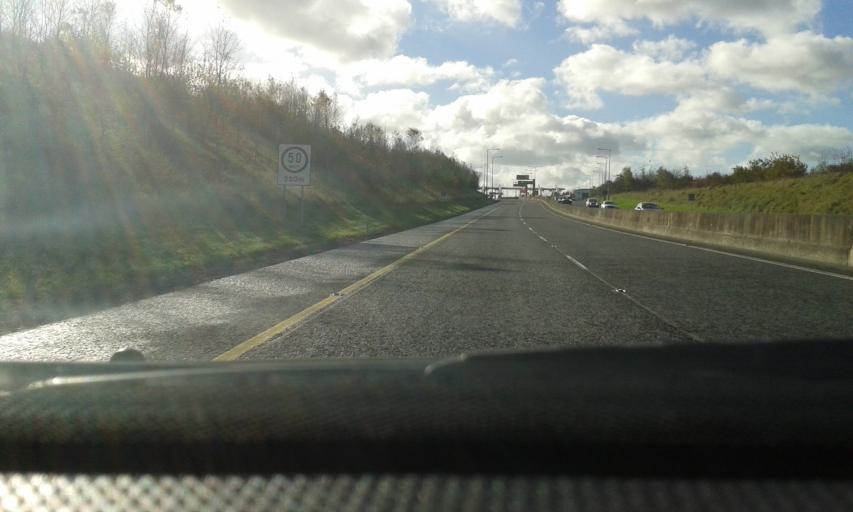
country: IE
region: Munster
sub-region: County Cork
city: Watergrasshill
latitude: 52.0307
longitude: -8.3231
